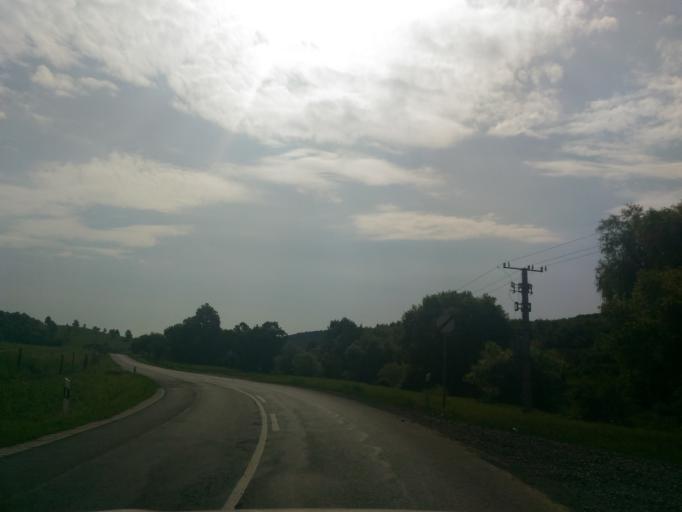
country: HU
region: Baranya
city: Komlo
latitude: 46.1609
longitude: 18.2157
